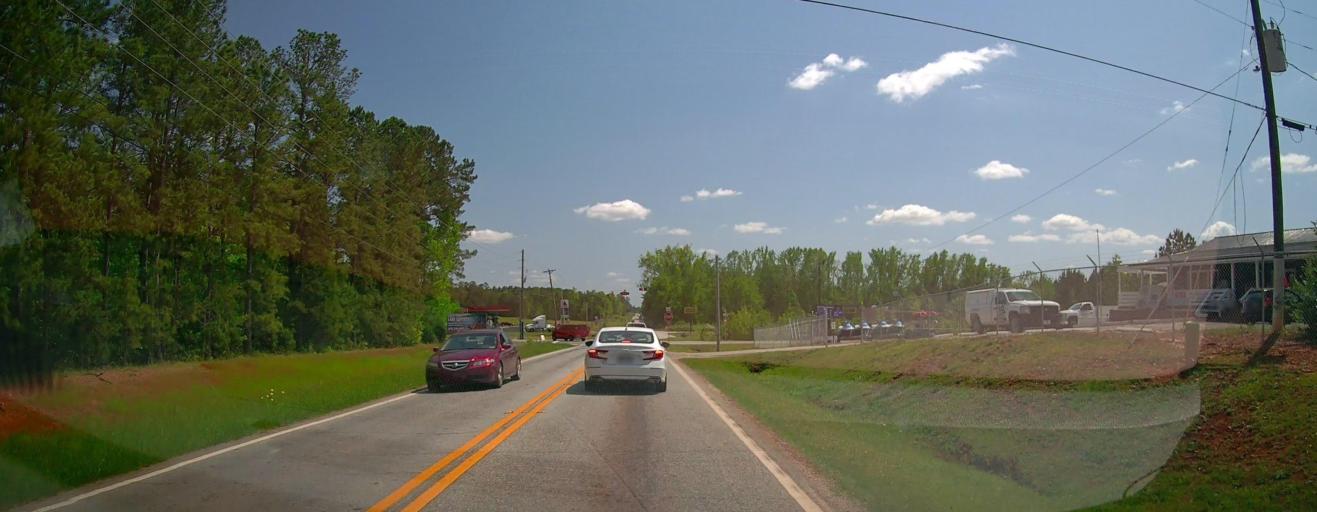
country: US
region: Georgia
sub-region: Putnam County
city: Eatonton
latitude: 33.2728
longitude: -83.3017
